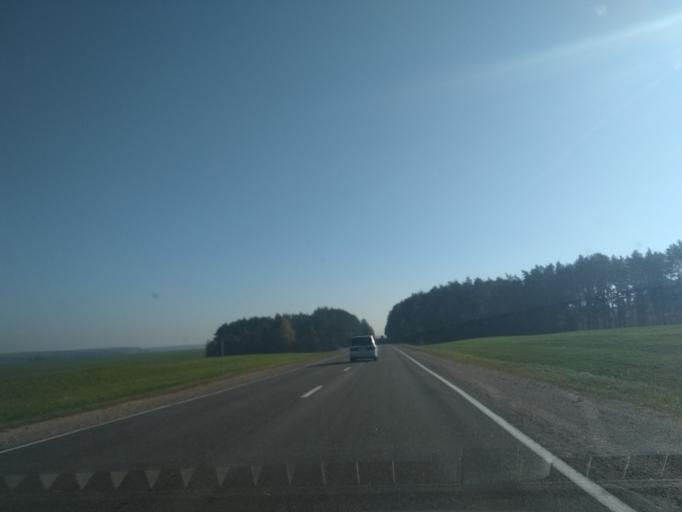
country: BY
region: Grodnenskaya
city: Zel'va
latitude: 53.1333
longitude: 24.9948
